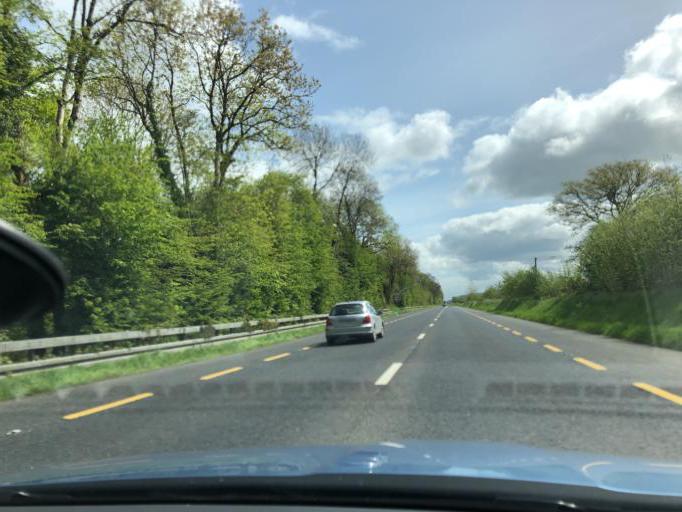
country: IE
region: Munster
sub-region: County Cork
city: Mallow
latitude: 52.1304
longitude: -8.7551
